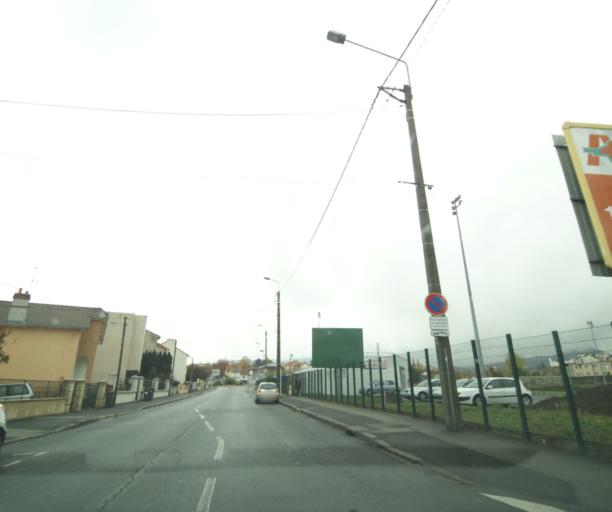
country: FR
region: Auvergne
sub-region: Departement du Puy-de-Dome
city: Aubiere
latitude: 45.7602
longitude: 3.1009
